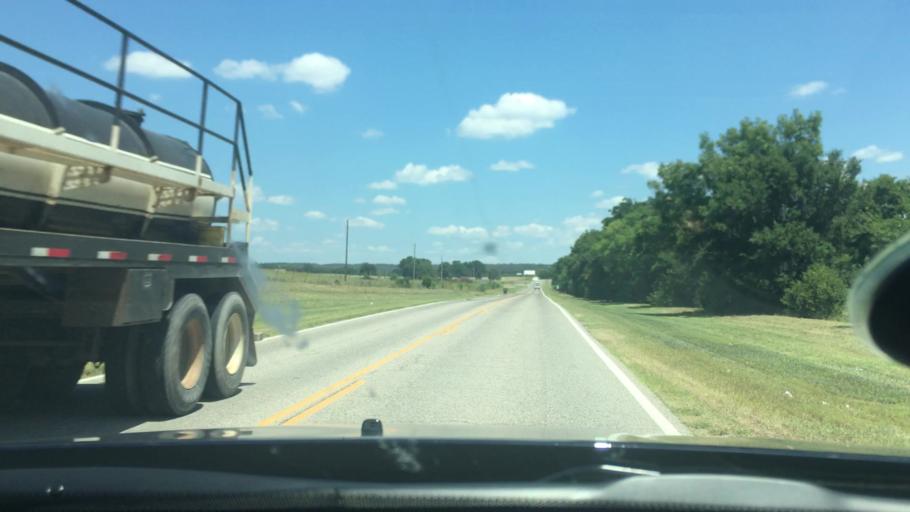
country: US
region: Oklahoma
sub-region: Carter County
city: Dickson
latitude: 34.2836
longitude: -96.9682
